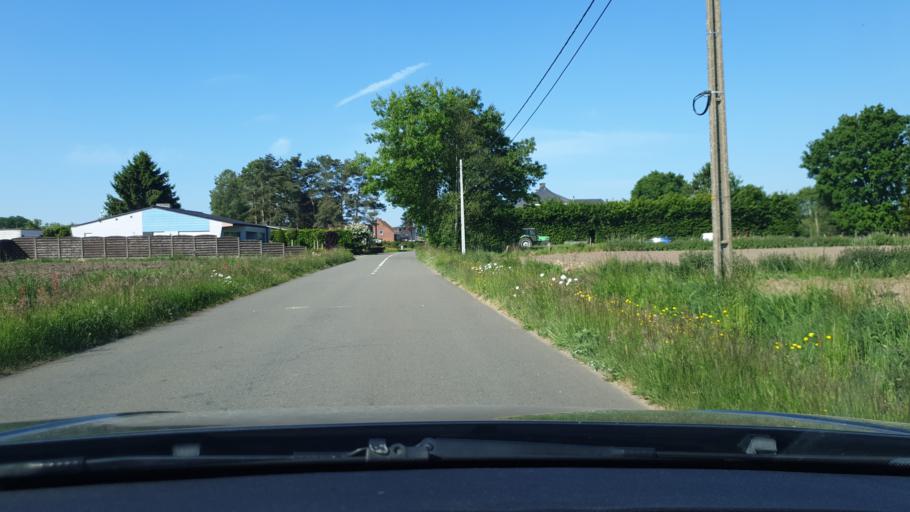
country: BE
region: Flanders
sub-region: Provincie Antwerpen
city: Geel
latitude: 51.1531
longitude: 4.9498
